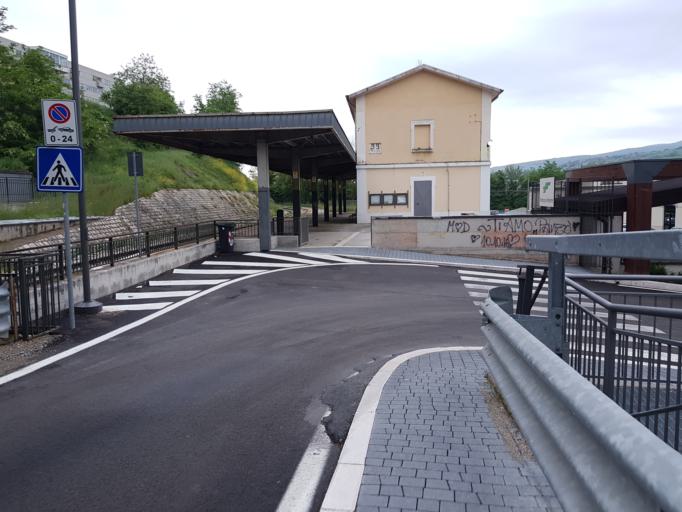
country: IT
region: Basilicate
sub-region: Provincia di Potenza
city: Potenza
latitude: 40.6300
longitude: 15.8062
